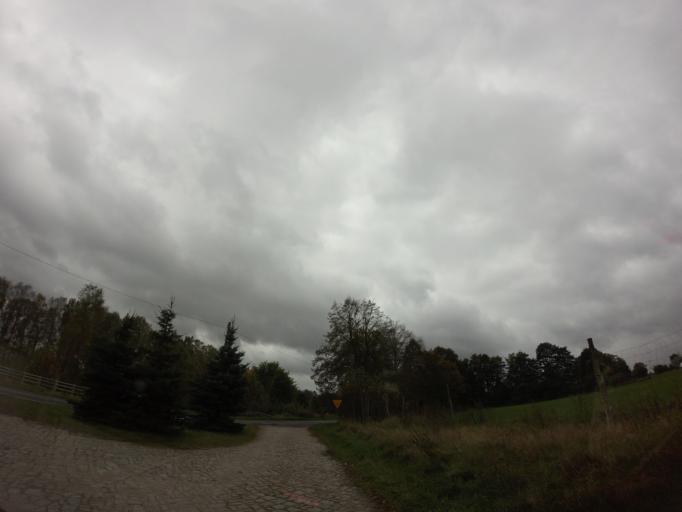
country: PL
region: West Pomeranian Voivodeship
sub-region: Powiat choszczenski
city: Drawno
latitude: 53.2260
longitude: 15.7893
